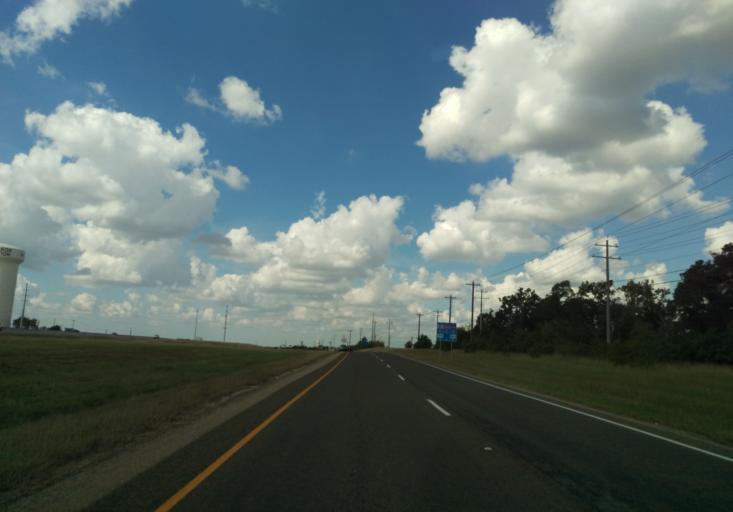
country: US
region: Texas
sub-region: Brazos County
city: College Station
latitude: 30.5573
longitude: -96.2547
